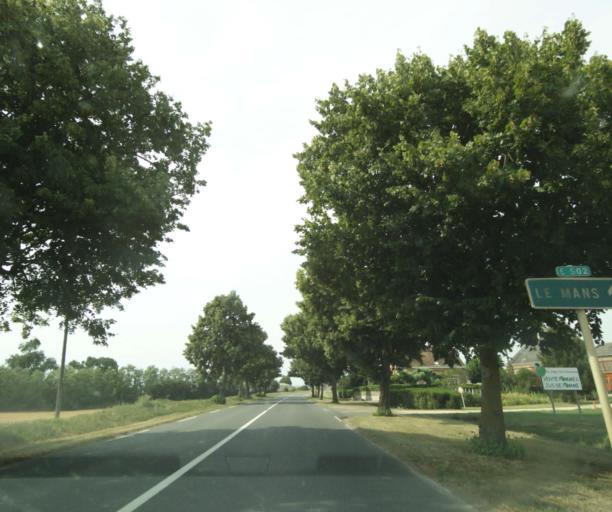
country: FR
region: Centre
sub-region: Departement d'Indre-et-Loire
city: Neuille-Pont-Pierre
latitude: 47.5524
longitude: 0.5493
